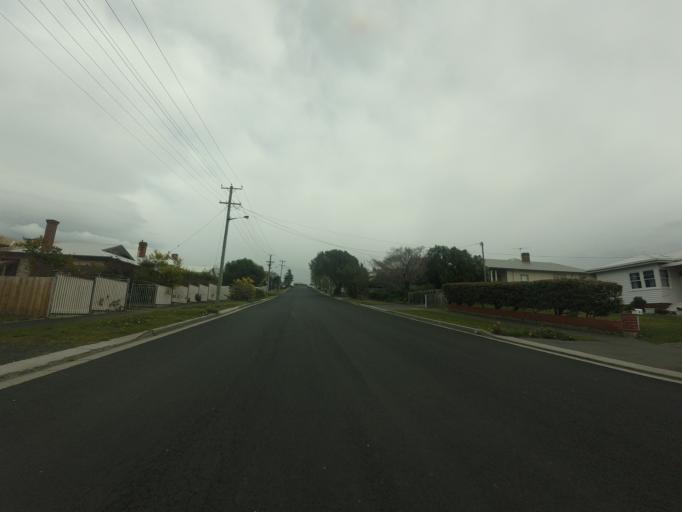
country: AU
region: Tasmania
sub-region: Clarence
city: Bellerive
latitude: -42.8775
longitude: 147.3688
